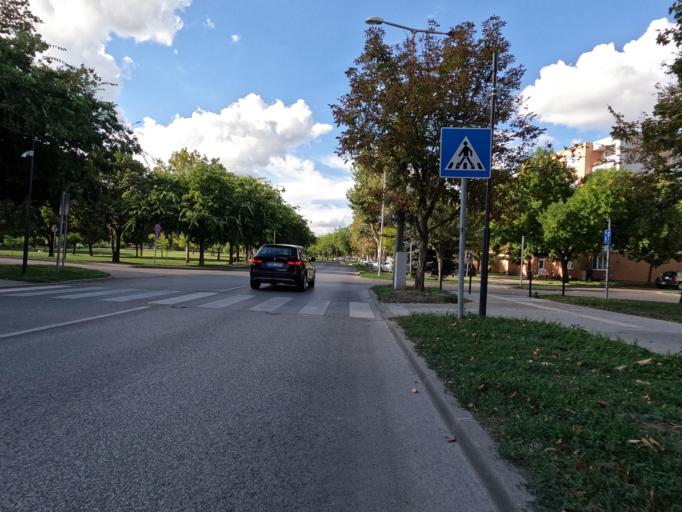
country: HU
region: Tolna
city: Paks
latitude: 46.6204
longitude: 18.8578
